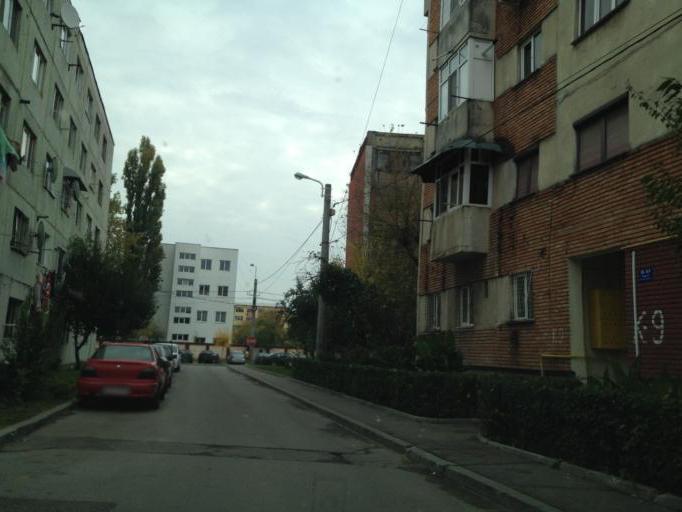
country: RO
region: Dolj
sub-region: Municipiul Craiova
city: Popoveni
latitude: 44.3014
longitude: 23.7909
